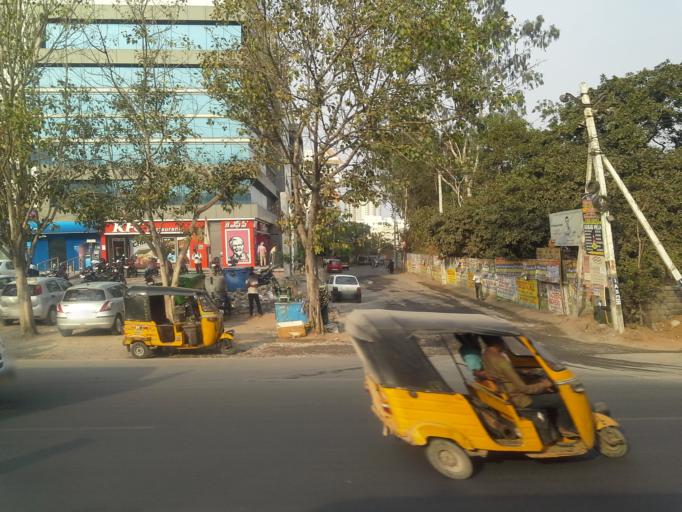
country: IN
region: Telangana
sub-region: Rangareddi
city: Kukatpalli
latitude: 17.4423
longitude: 78.3572
